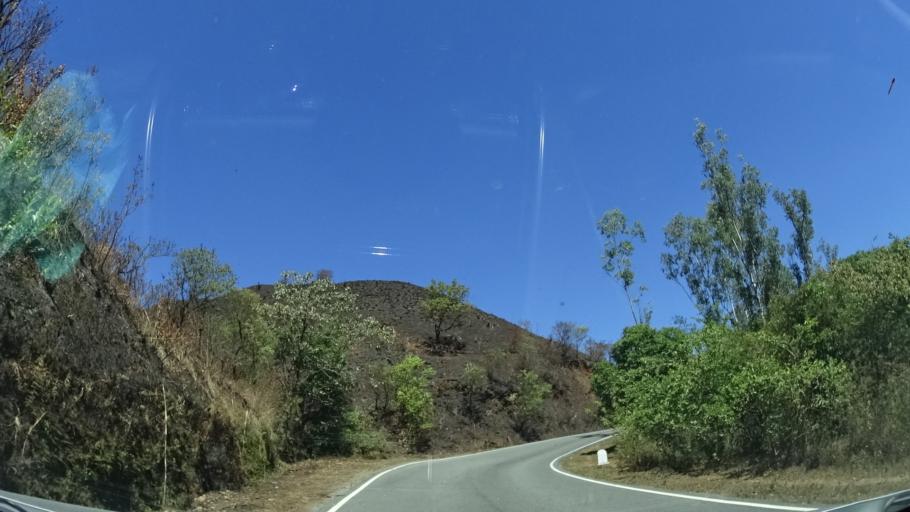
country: IN
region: Karnataka
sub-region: Chikmagalur
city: Sringeri
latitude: 13.2151
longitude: 75.2310
